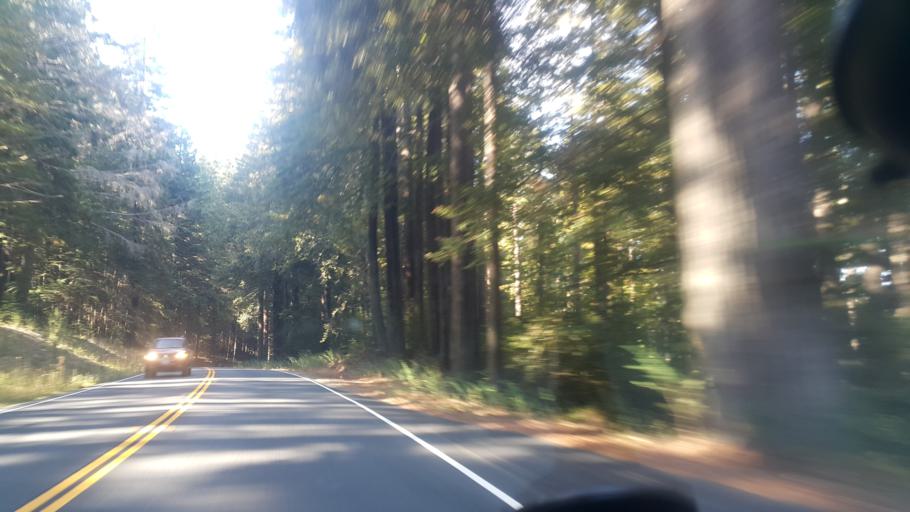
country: US
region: California
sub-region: Mendocino County
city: Fort Bragg
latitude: 39.3588
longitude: -123.6484
